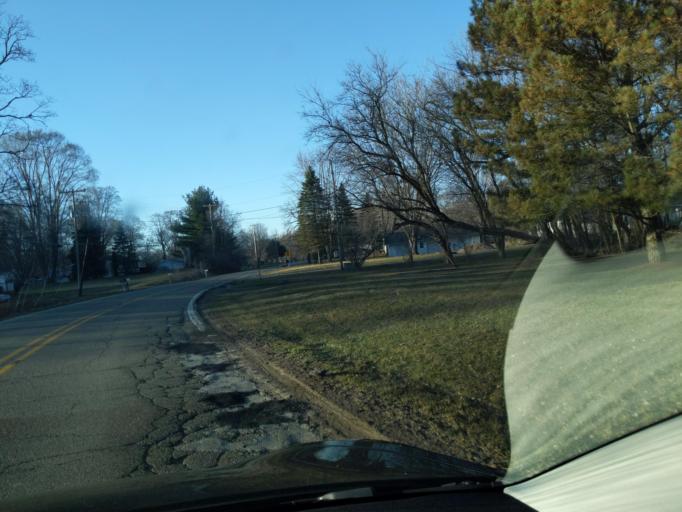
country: US
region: Michigan
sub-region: Livingston County
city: Pinckney
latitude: 42.4265
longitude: -84.0563
